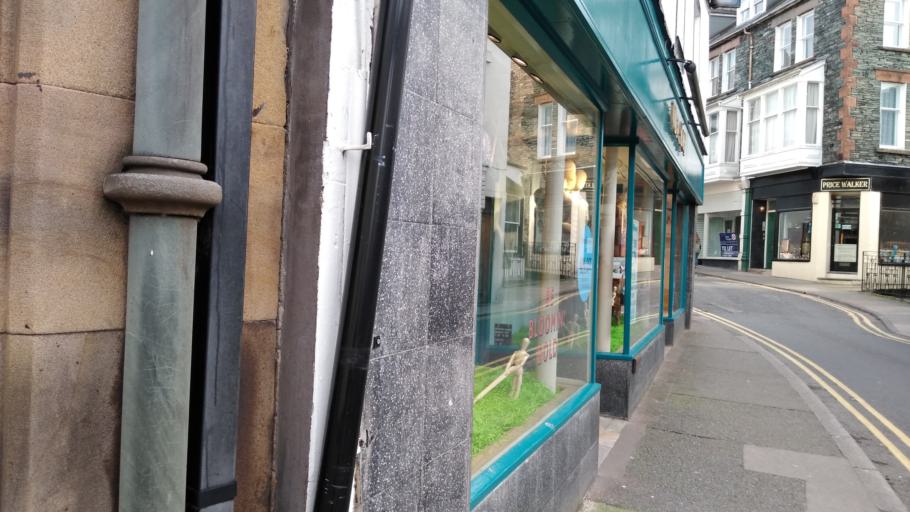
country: GB
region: England
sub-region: Cumbria
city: Keswick
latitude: 54.6004
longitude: -3.1362
